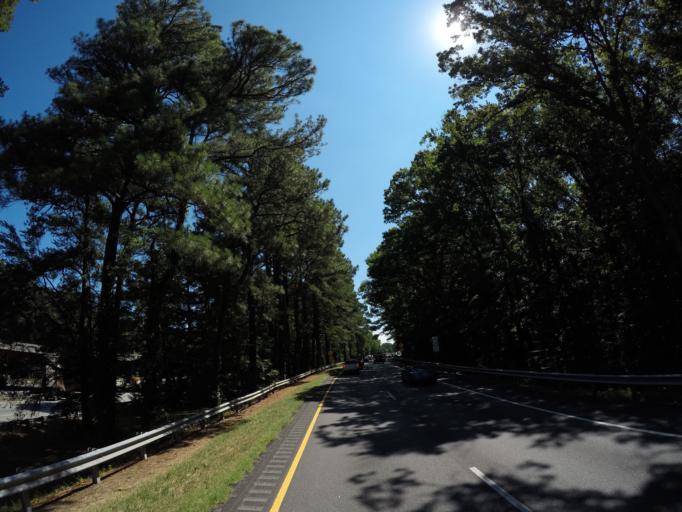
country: US
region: Maryland
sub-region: Queen Anne's County
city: Grasonville
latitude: 38.9807
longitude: -76.1684
